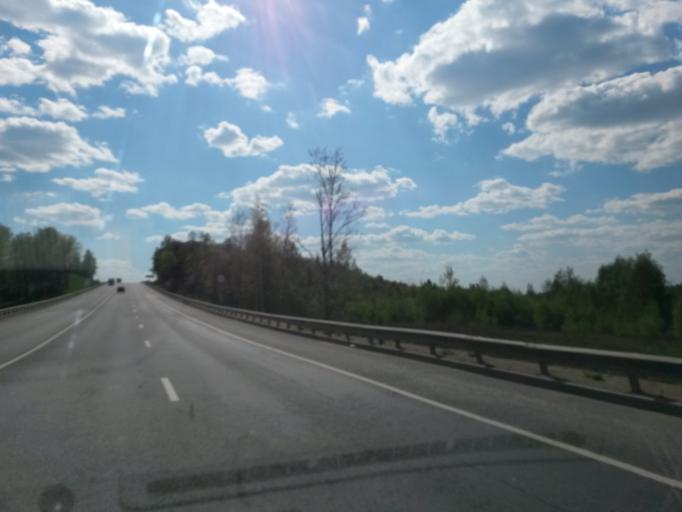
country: RU
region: Jaroslavl
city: Petrovsk
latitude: 56.9710
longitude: 39.2049
